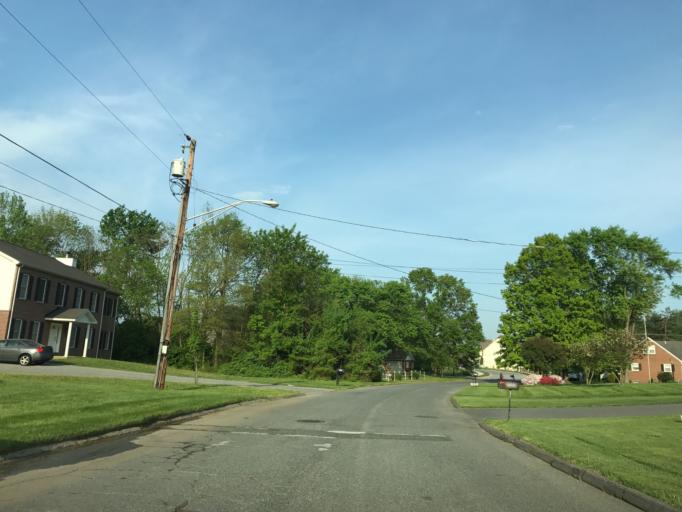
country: US
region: Maryland
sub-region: Baltimore County
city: White Marsh
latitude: 39.3714
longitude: -76.4189
